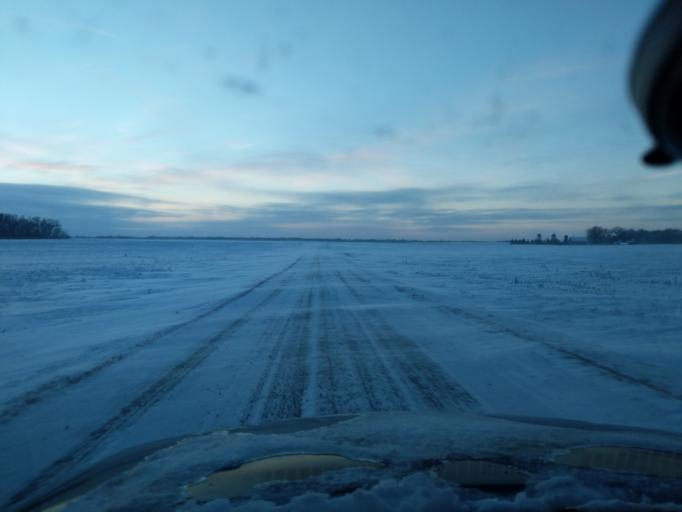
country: US
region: Minnesota
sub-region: Renville County
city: Renville
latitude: 44.7271
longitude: -95.3489
